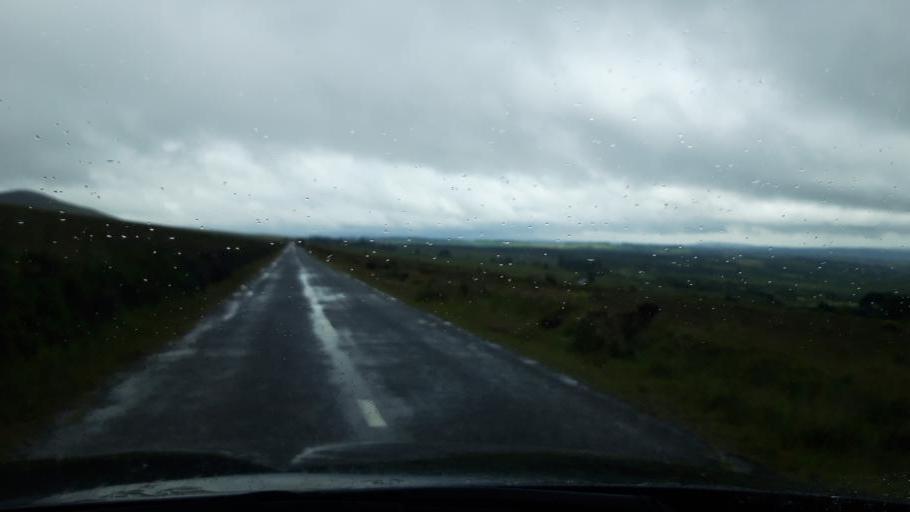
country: IE
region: Munster
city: Cahir
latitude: 52.2167
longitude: -7.9339
